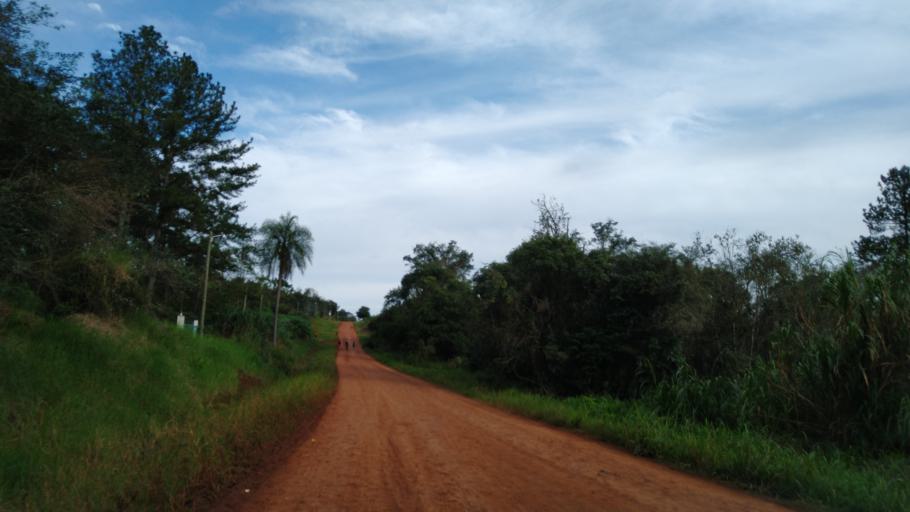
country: AR
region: Misiones
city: Capiovi
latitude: -26.9380
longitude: -55.0967
